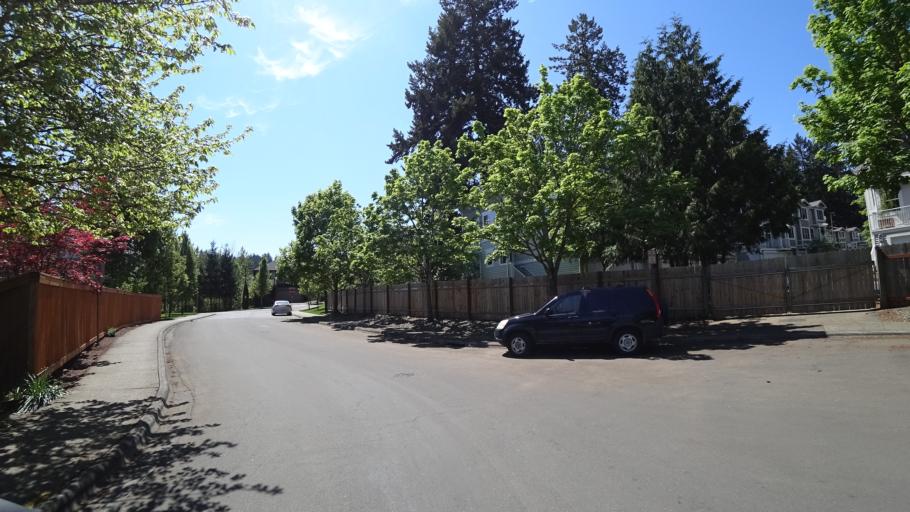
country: US
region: Oregon
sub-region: Washington County
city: King City
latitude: 45.4335
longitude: -122.8209
